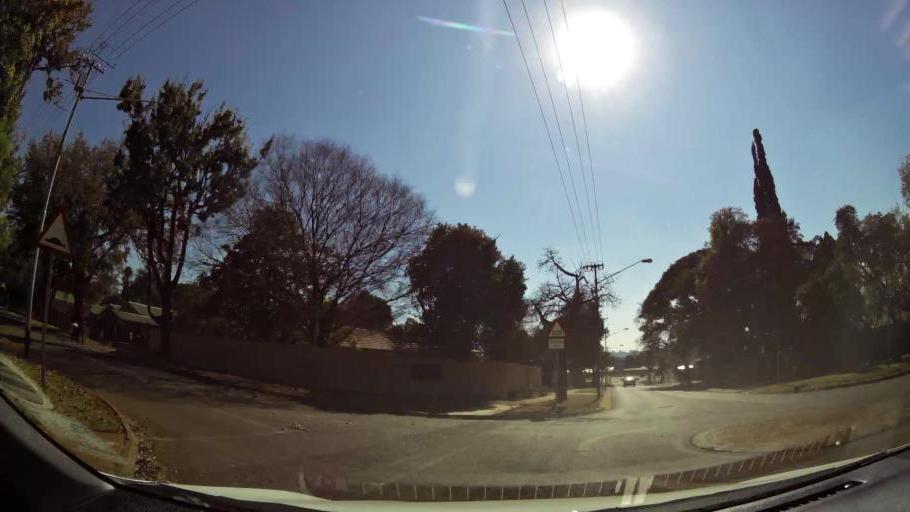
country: ZA
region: Gauteng
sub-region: City of Tshwane Metropolitan Municipality
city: Pretoria
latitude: -25.7739
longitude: 28.2194
